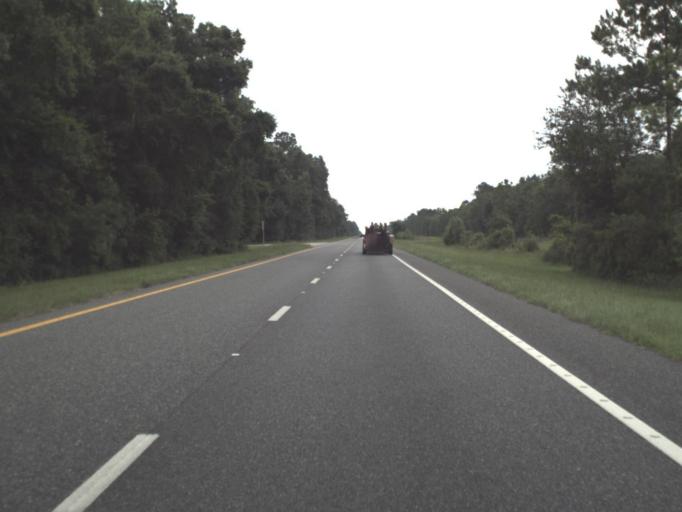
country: US
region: Florida
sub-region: Levy County
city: Bronson
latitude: 29.2696
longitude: -82.7331
